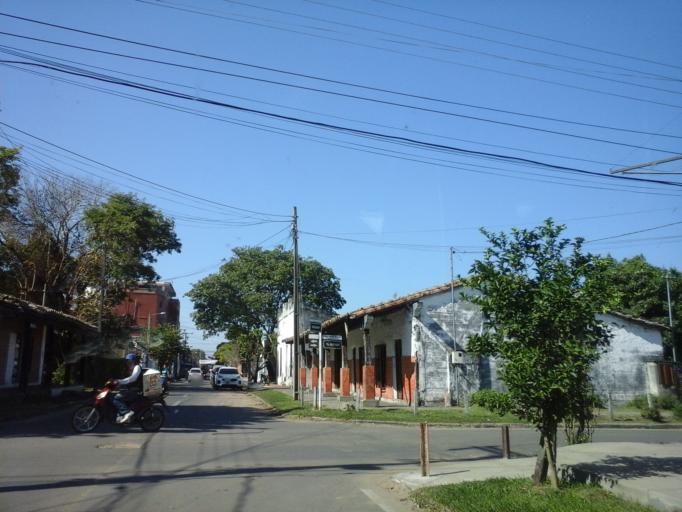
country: PY
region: Neembucu
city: Pilar
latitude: -26.8570
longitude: -58.3088
